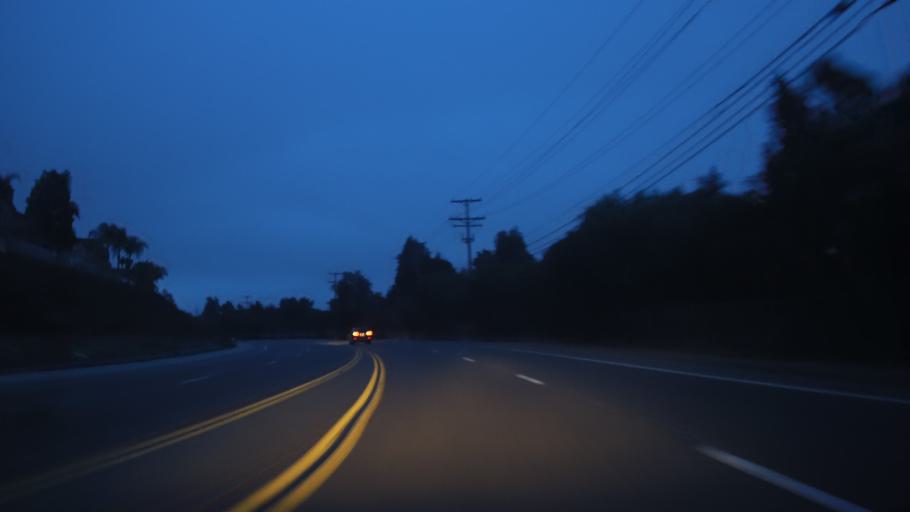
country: US
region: California
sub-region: San Diego County
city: Rancho San Diego
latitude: 32.7428
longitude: -116.9238
